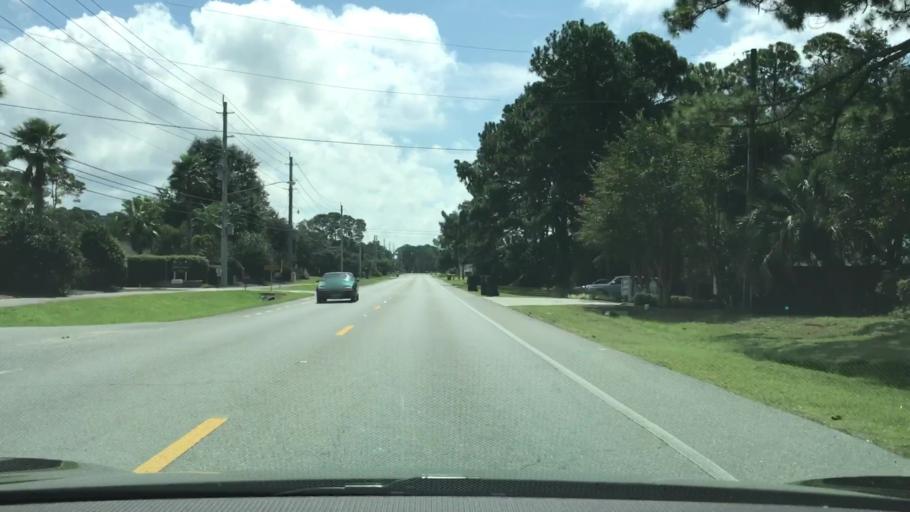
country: US
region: Florida
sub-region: Bay County
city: Lower Grand Lagoon
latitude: 30.1590
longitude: -85.7612
